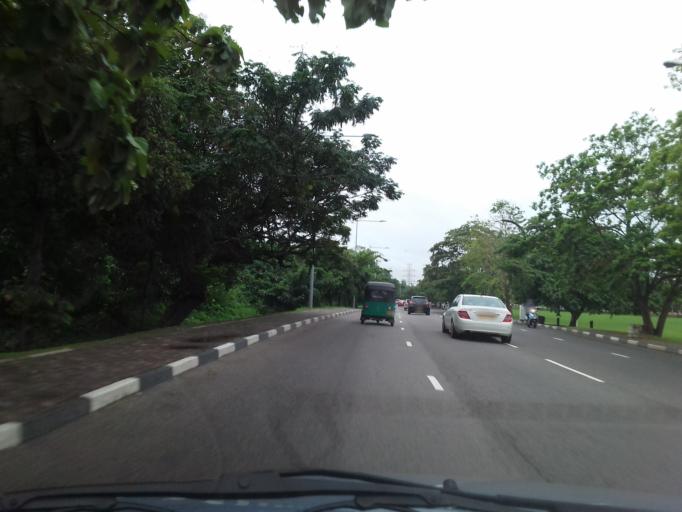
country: LK
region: Western
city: Battaramulla South
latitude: 6.8937
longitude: 79.9193
